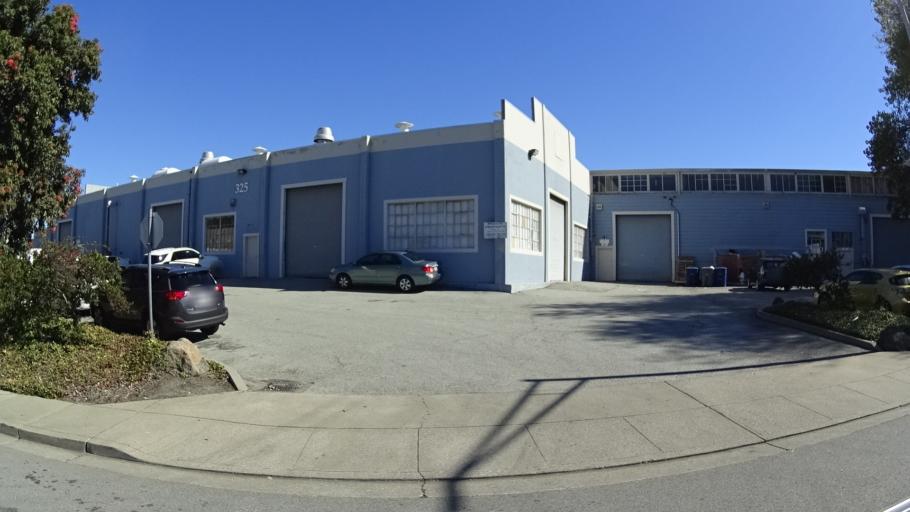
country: US
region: California
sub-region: San Mateo County
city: San Bruno
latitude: 37.6420
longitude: -122.4177
